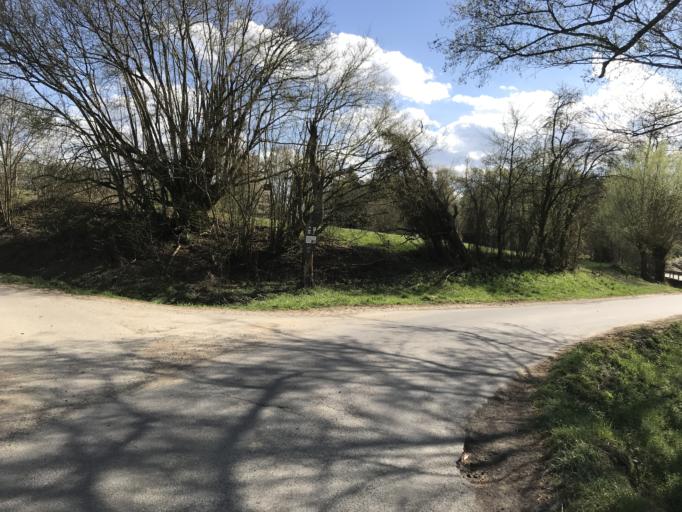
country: DE
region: Hesse
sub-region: Regierungsbezirk Giessen
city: Rabenau
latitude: 50.6750
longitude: 8.8323
